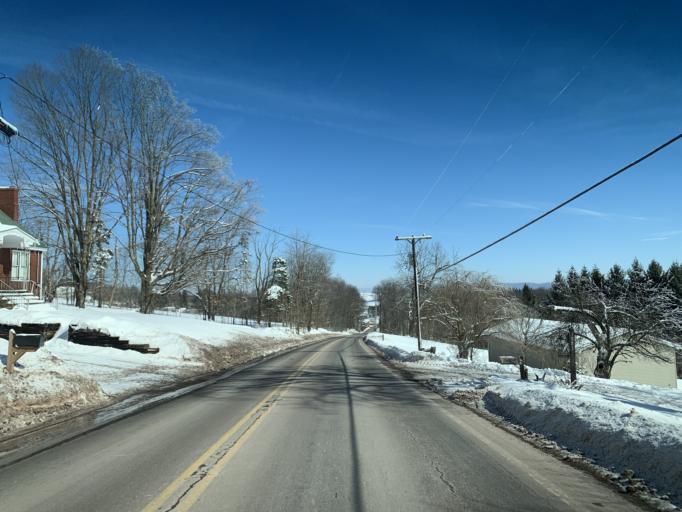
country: US
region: Pennsylvania
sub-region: Somerset County
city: Meyersdale
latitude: 39.7299
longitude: -79.1547
